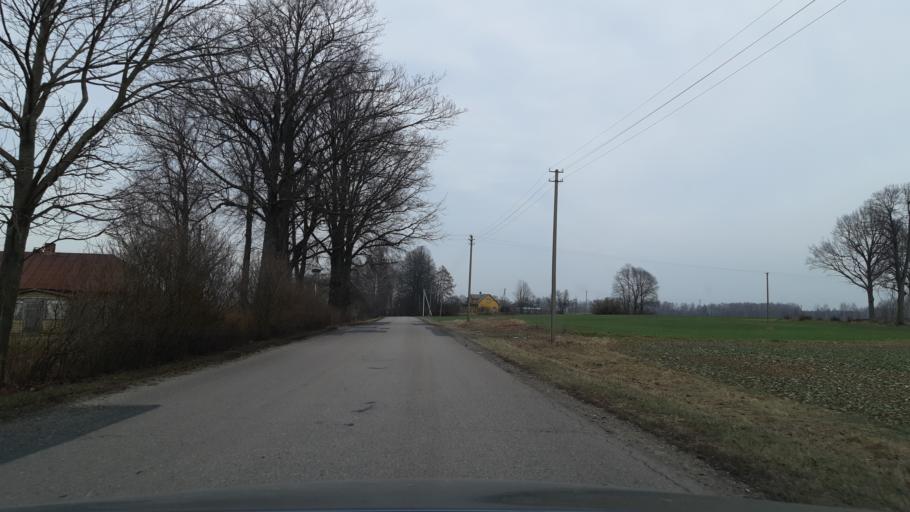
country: LT
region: Marijampoles apskritis
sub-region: Marijampole Municipality
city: Marijampole
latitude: 54.7214
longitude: 23.3355
